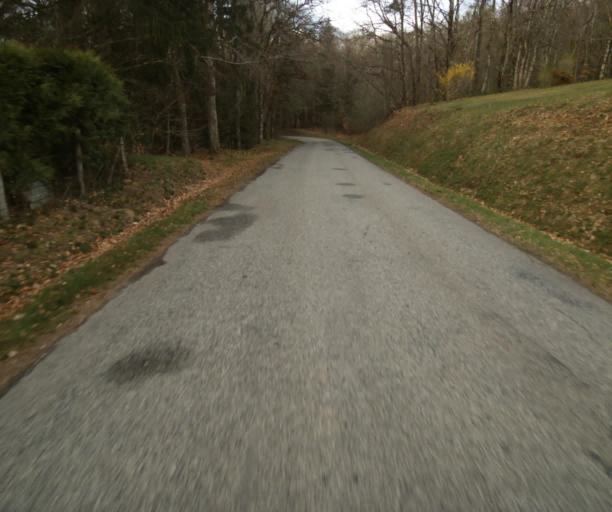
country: FR
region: Limousin
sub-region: Departement de la Correze
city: Argentat
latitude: 45.2243
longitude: 1.9782
